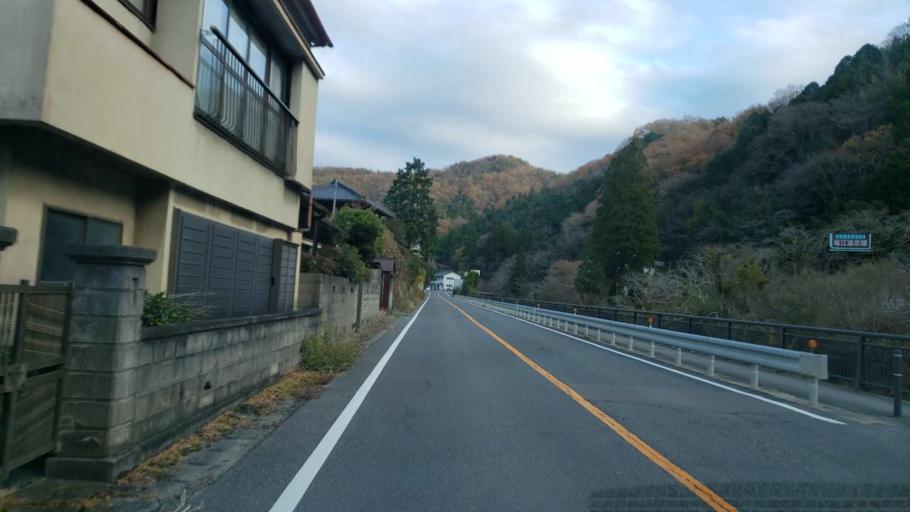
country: JP
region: Tokushima
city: Wakimachi
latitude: 34.1694
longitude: 134.0832
